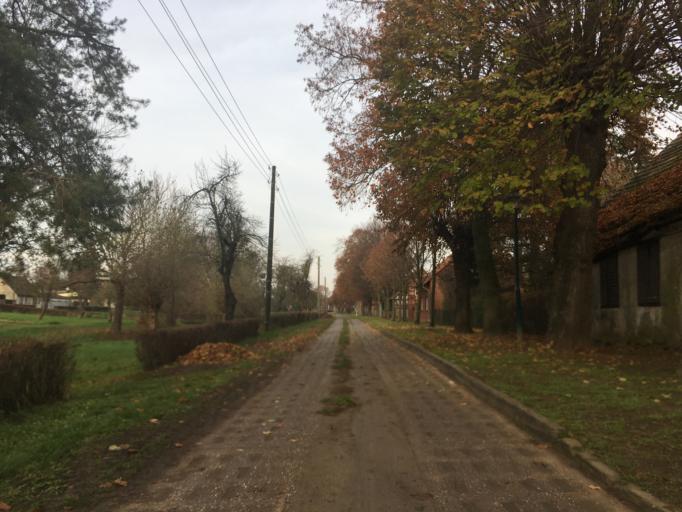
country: DE
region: Brandenburg
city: Neulewin
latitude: 52.7279
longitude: 14.2795
